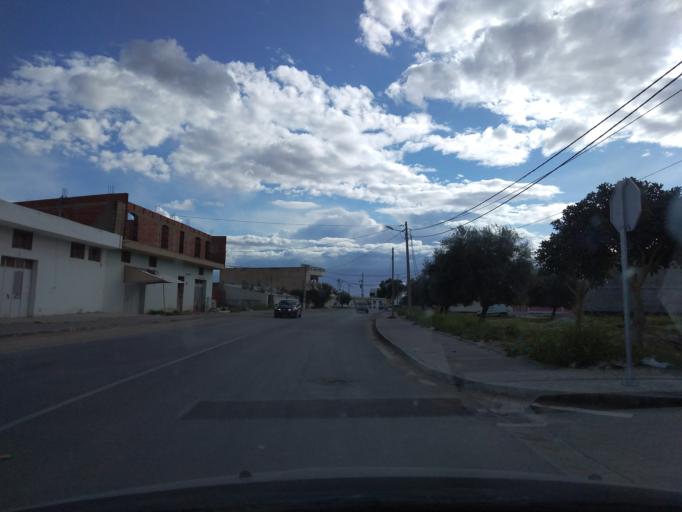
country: TN
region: Susah
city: Masakin
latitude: 35.7166
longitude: 10.5640
